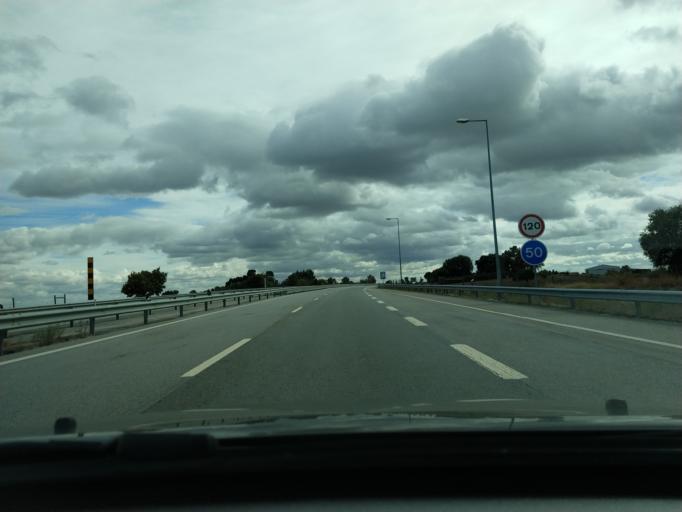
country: PT
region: Guarda
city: Alcains
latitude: 40.0244
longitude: -7.4663
